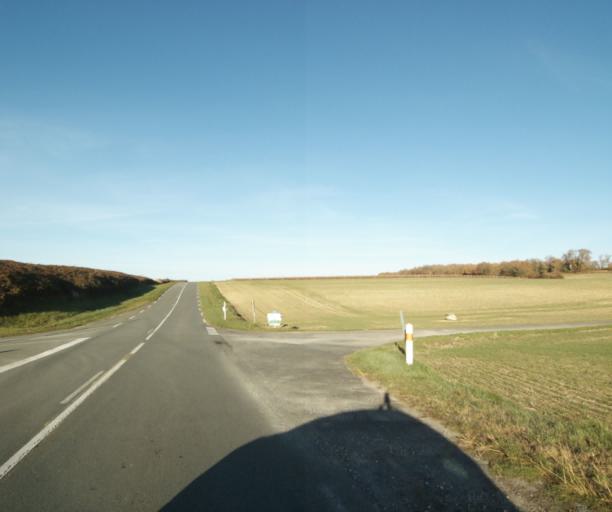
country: FR
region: Poitou-Charentes
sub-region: Departement de la Charente-Maritime
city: Cherac
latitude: 45.7026
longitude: -0.4701
